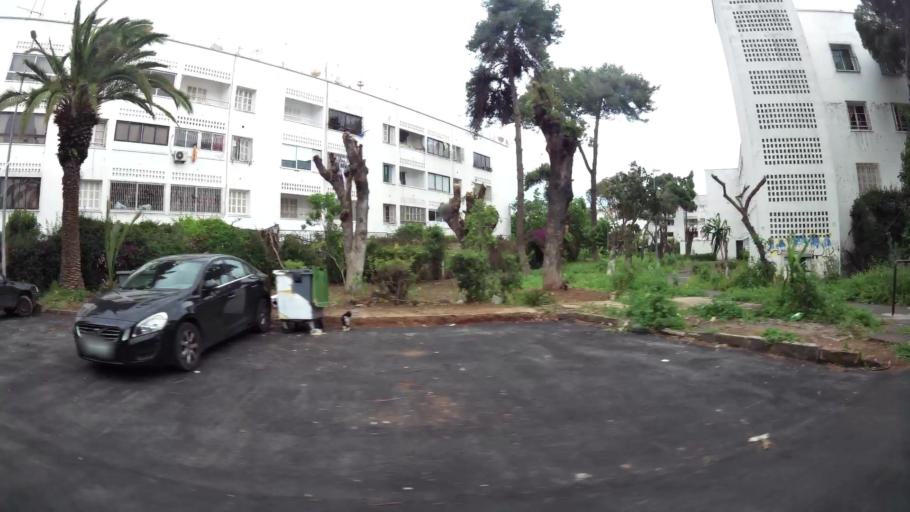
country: MA
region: Grand Casablanca
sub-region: Casablanca
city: Casablanca
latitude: 33.5650
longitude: -7.6410
